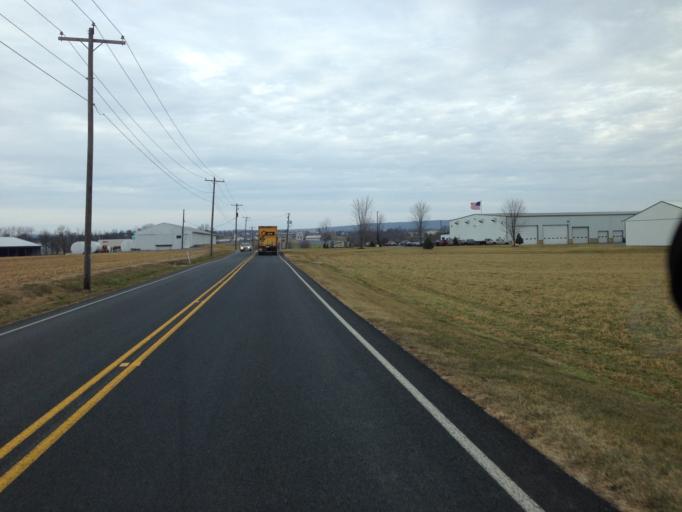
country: US
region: Pennsylvania
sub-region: Lancaster County
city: Manheim
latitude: 40.1631
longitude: -76.3669
